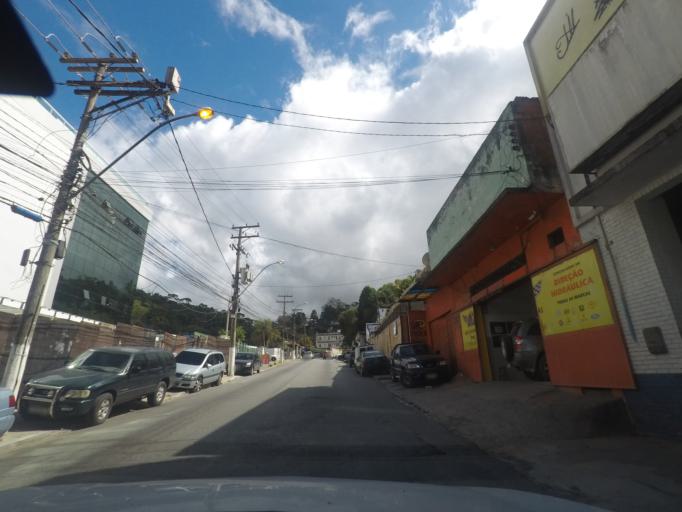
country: BR
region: Rio de Janeiro
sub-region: Teresopolis
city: Teresopolis
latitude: -22.3992
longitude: -42.9608
